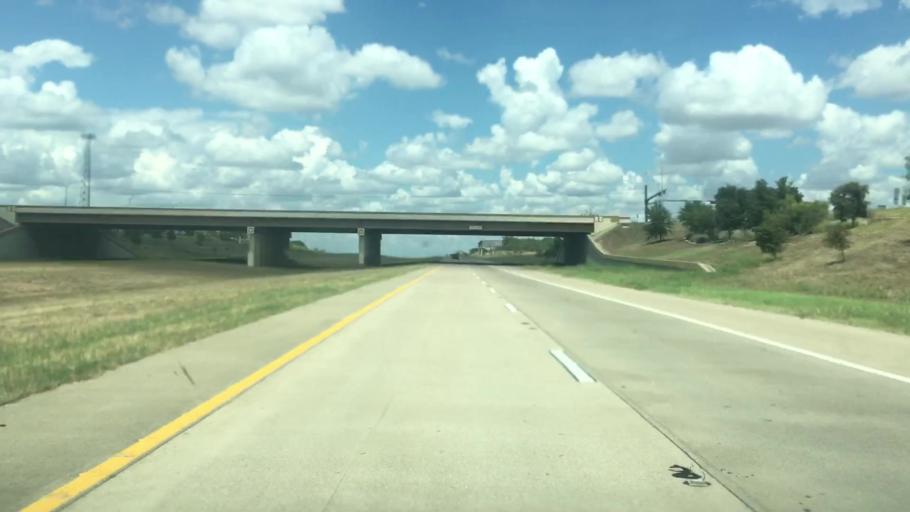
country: US
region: Texas
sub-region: Williamson County
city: Georgetown
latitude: 30.6411
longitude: -97.6295
